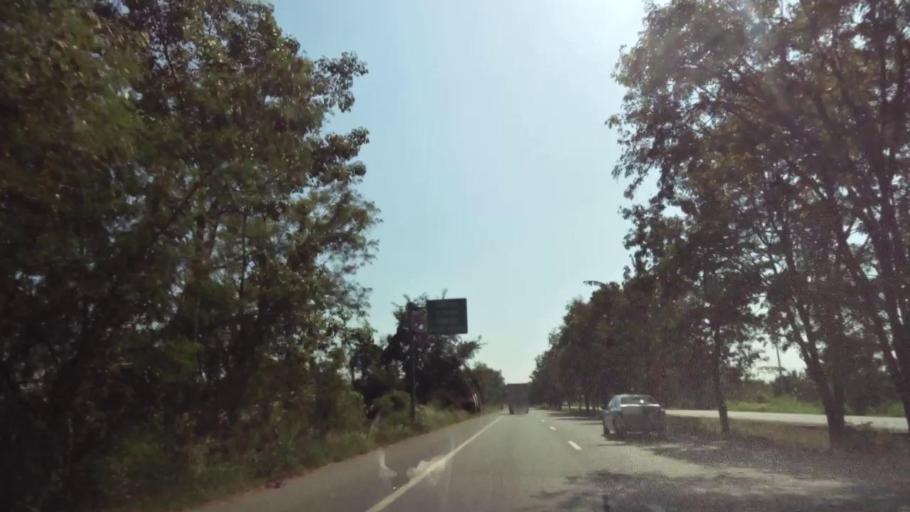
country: TH
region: Nakhon Sawan
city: Kao Liao
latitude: 15.9076
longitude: 100.1125
